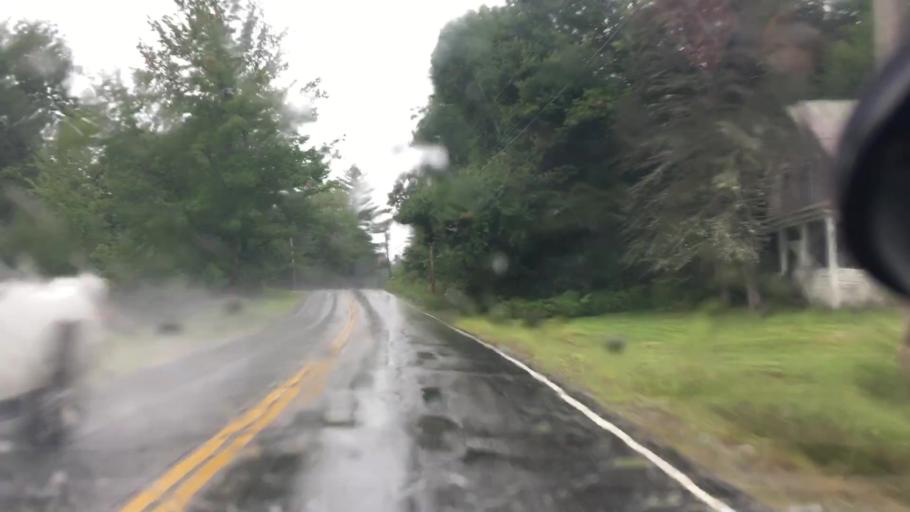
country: US
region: Maine
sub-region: Oxford County
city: Lovell
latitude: 44.2542
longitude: -70.8213
